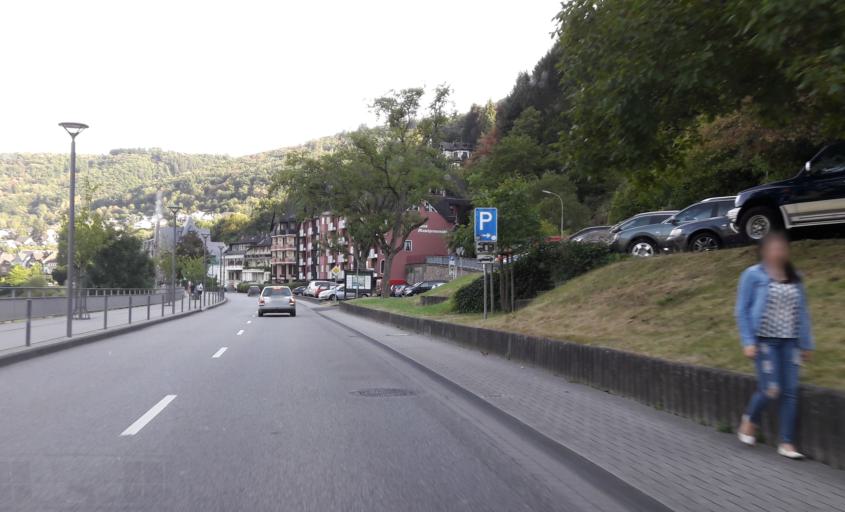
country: DE
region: Rheinland-Pfalz
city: Cochem
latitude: 50.1408
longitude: 7.1696
